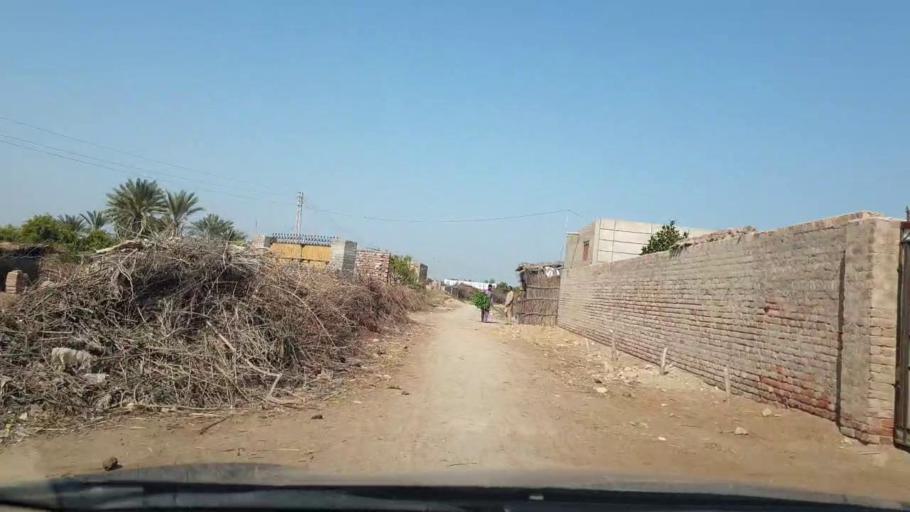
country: PK
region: Sindh
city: Mirpur Khas
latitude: 25.6145
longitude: 68.8943
